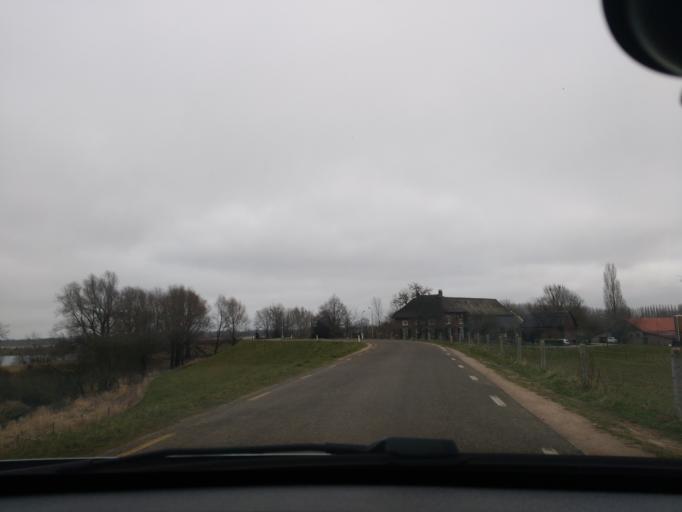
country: NL
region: Gelderland
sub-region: Gemeente Groesbeek
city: Berg en Dal
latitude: 51.8636
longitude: 5.9312
